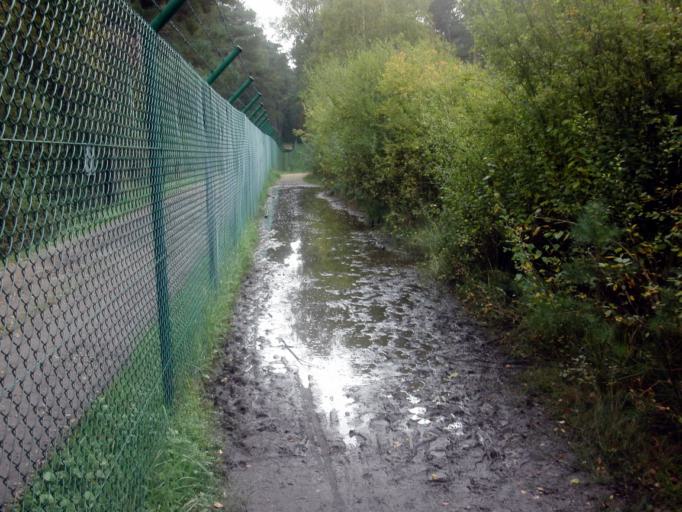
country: DE
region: North Rhine-Westphalia
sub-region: Regierungsbezirk Koln
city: Gangelt
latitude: 50.9490
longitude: 6.0420
